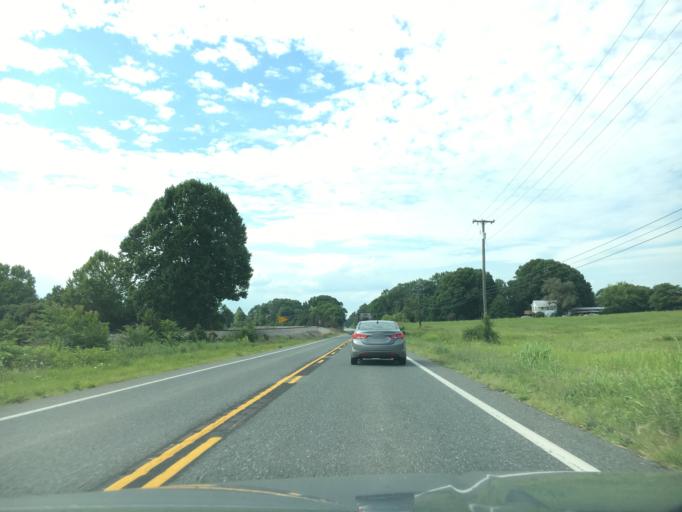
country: US
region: Virginia
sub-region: Campbell County
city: Brookneal
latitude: 37.0818
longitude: -78.9863
